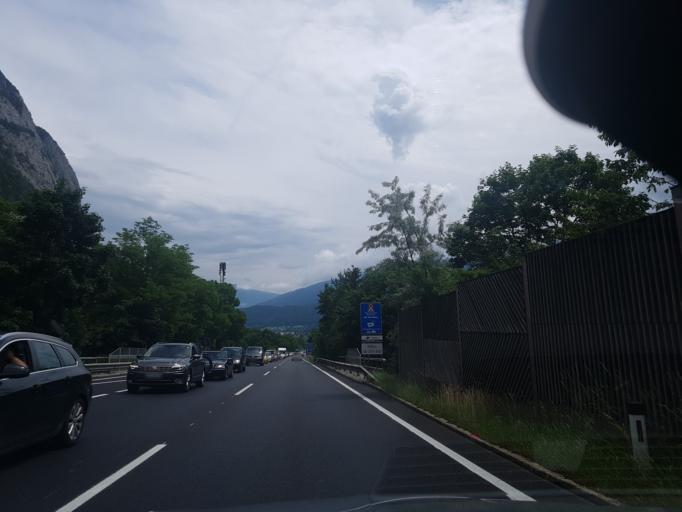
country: AT
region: Tyrol
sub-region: Politischer Bezirk Innsbruck Land
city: Unterperfuss
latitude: 47.2731
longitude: 11.2541
